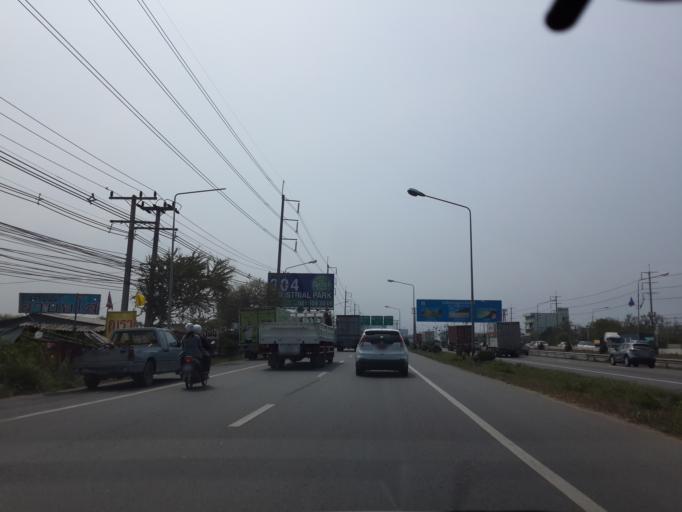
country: TH
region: Chon Buri
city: Chon Buri
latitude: 13.4401
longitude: 101.0010
